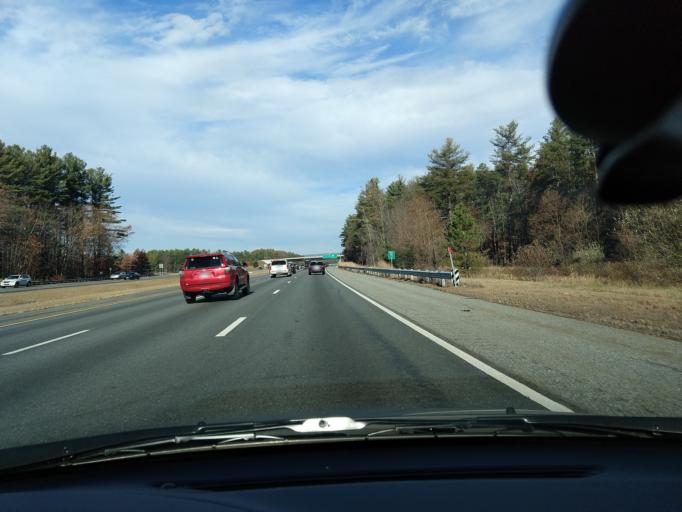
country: US
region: Massachusetts
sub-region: Middlesex County
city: Tyngsboro
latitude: 42.6764
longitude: -71.4400
